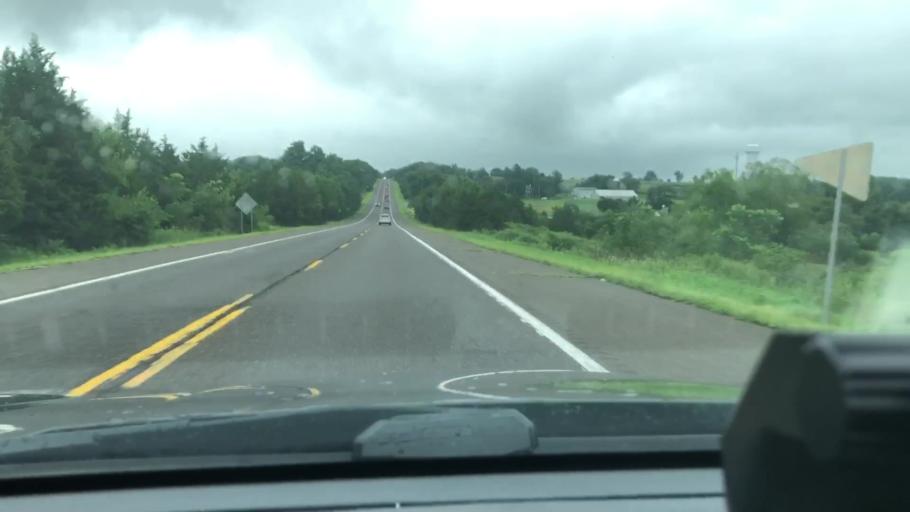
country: US
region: Pennsylvania
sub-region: Bucks County
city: Spinnerstown
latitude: 40.4245
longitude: -75.4406
